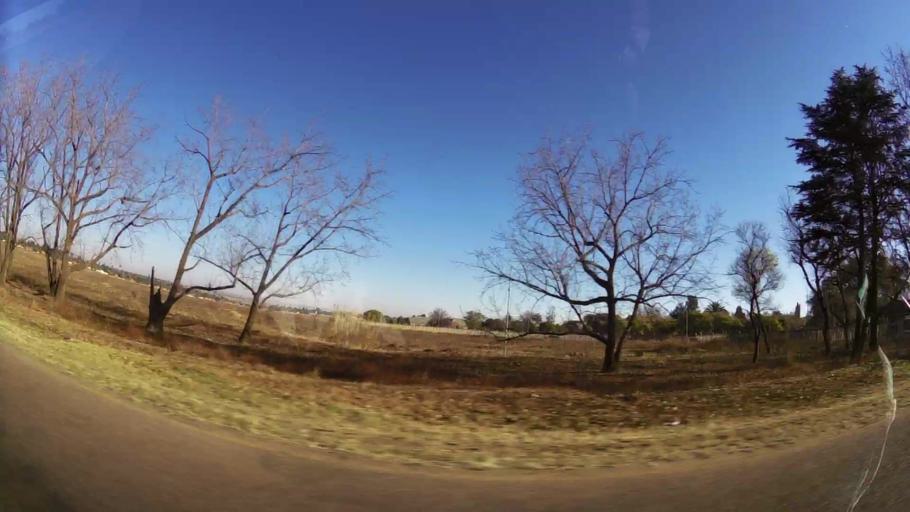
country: ZA
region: Gauteng
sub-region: Ekurhuleni Metropolitan Municipality
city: Tembisa
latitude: -26.0428
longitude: 28.2464
